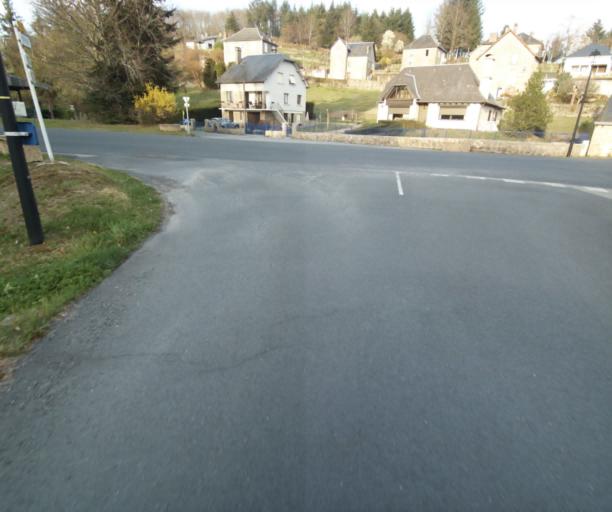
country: FR
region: Limousin
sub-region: Departement de la Correze
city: Correze
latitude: 45.3735
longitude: 1.8770
